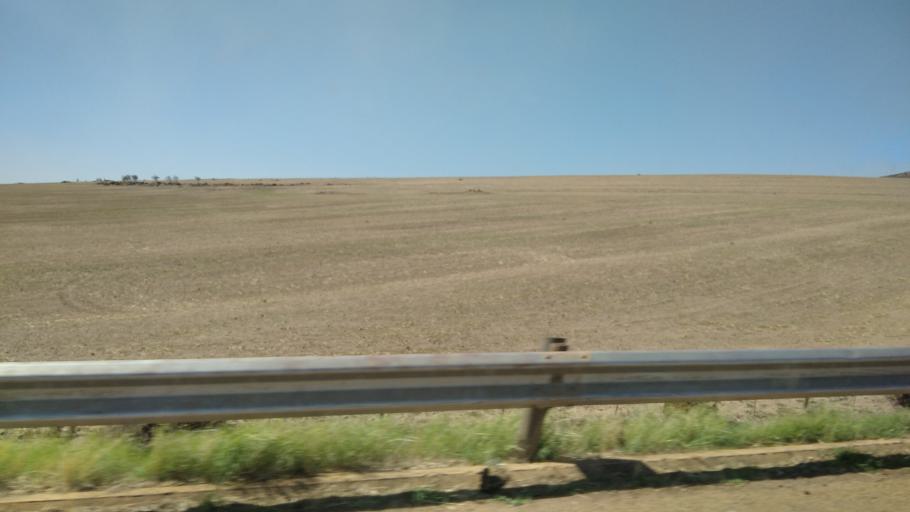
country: ZA
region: Western Cape
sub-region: West Coast District Municipality
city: Malmesbury
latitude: -33.3740
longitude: 18.6595
